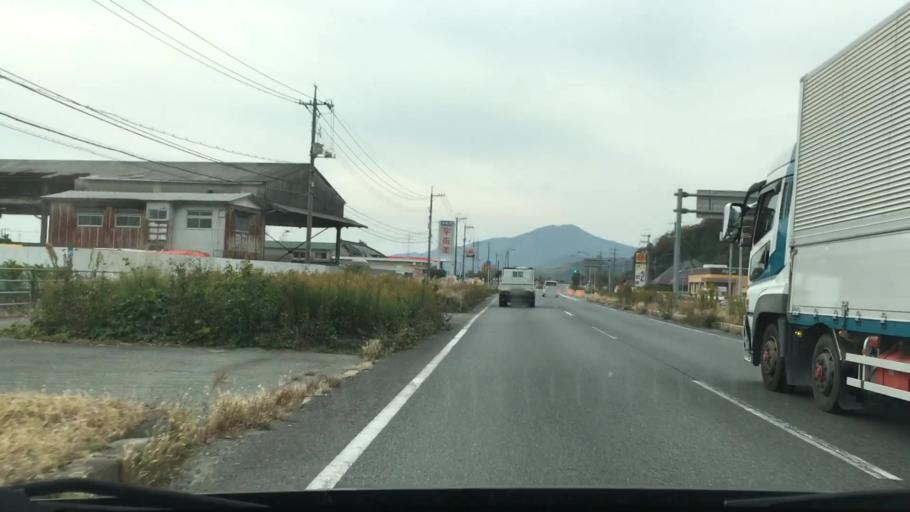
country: JP
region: Yamaguchi
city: Hofu
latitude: 34.0479
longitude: 131.5115
